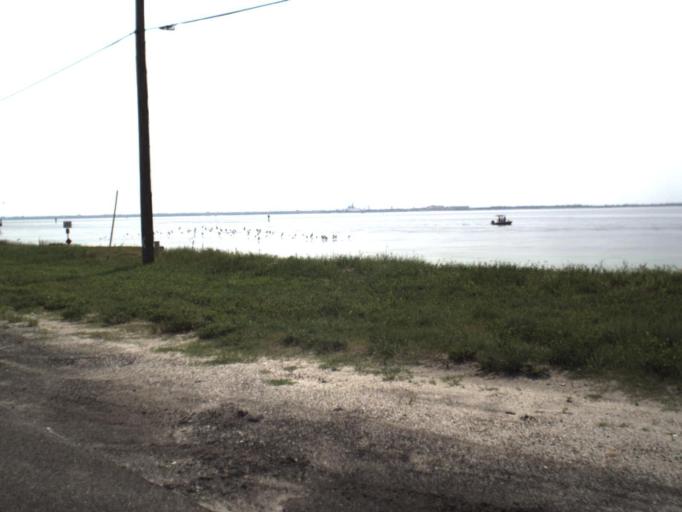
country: US
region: Florida
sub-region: Pinellas County
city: Gandy
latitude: 27.8766
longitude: -82.5926
